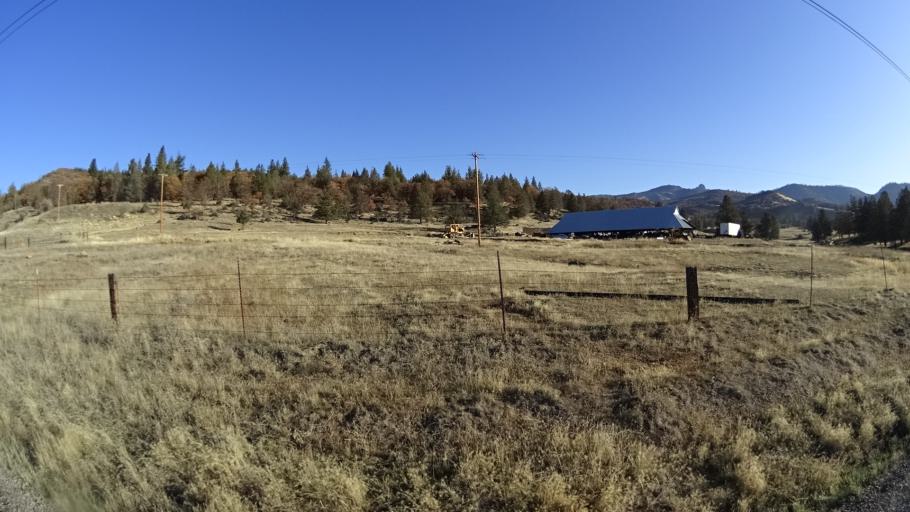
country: US
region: Oregon
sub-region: Jackson County
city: Ashland
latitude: 42.0011
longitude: -122.6380
